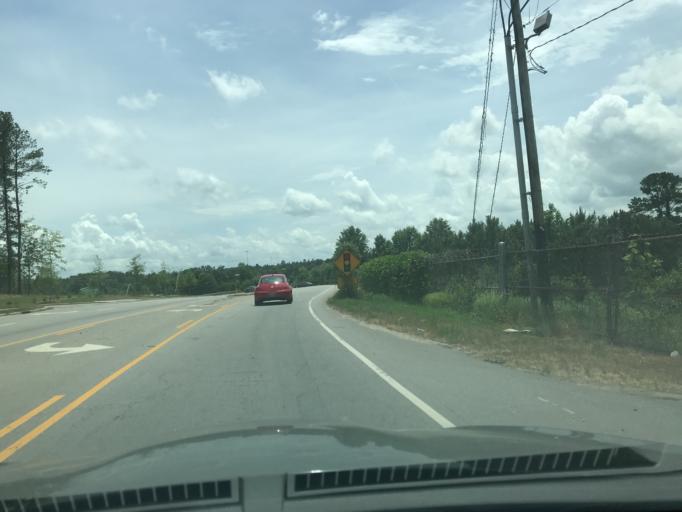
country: US
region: North Carolina
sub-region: Wake County
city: Wake Forest
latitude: 35.8820
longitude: -78.5743
